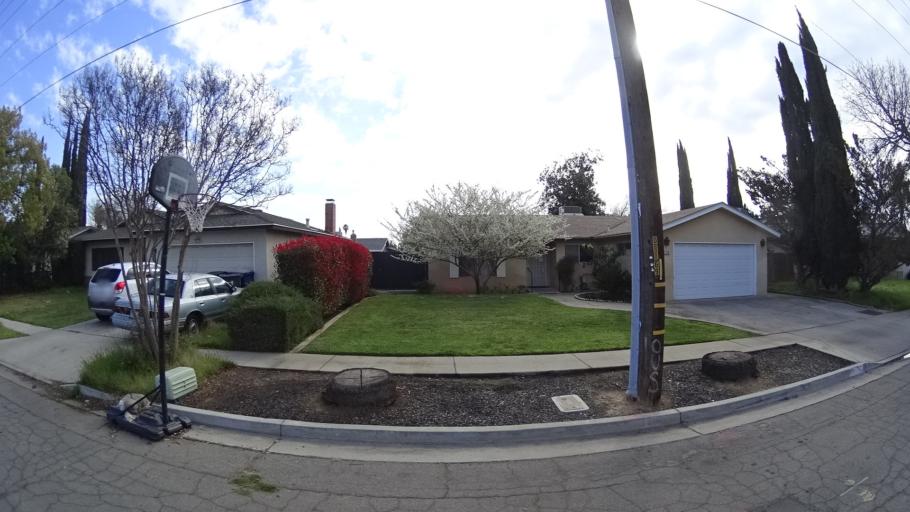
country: US
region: California
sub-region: Fresno County
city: Clovis
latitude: 36.8360
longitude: -119.7632
